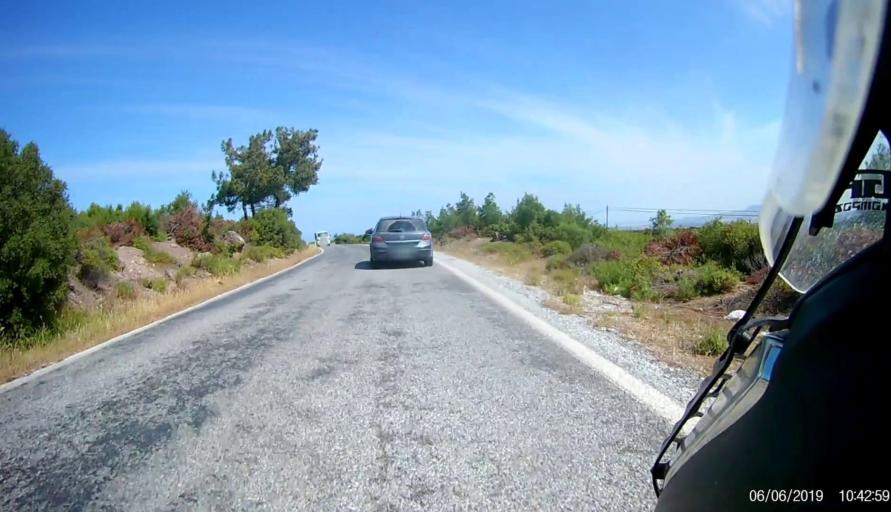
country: TR
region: Canakkale
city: Ayvacik
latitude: 39.5096
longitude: 26.4259
